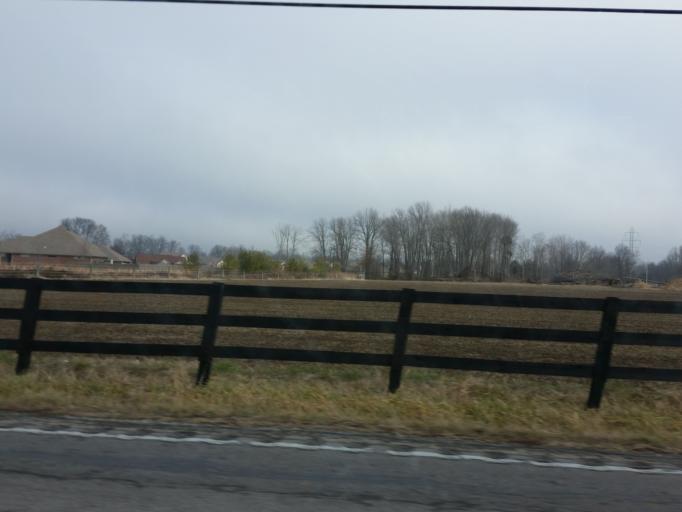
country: US
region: Indiana
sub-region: Jefferson County
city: North Madison
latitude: 38.7846
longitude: -85.4283
